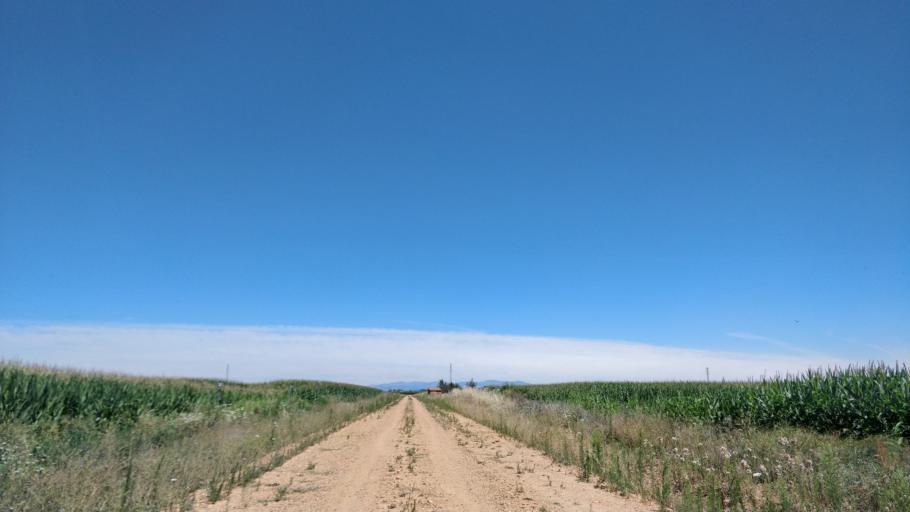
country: ES
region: Castille and Leon
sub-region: Provincia de Leon
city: Bustillo del Paramo
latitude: 42.4556
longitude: -5.8166
